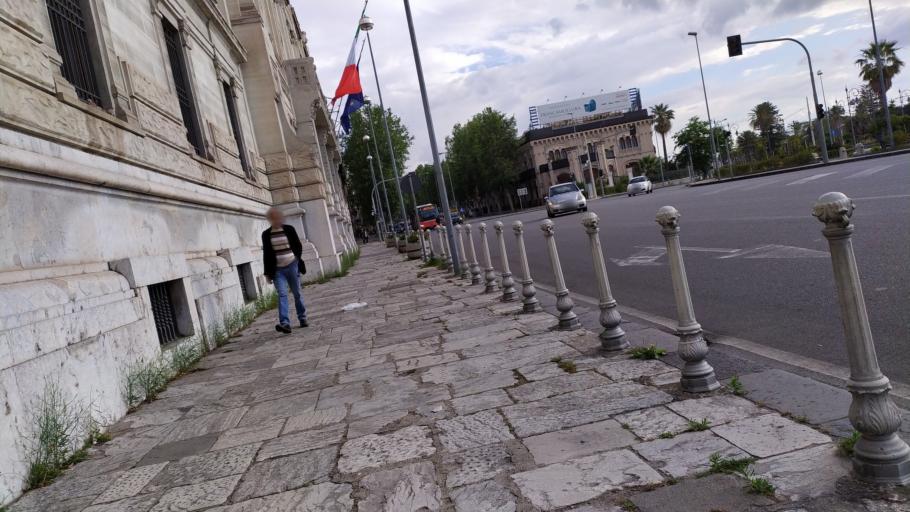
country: IT
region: Sicily
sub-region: Messina
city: Messina
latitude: 38.1990
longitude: 15.5573
